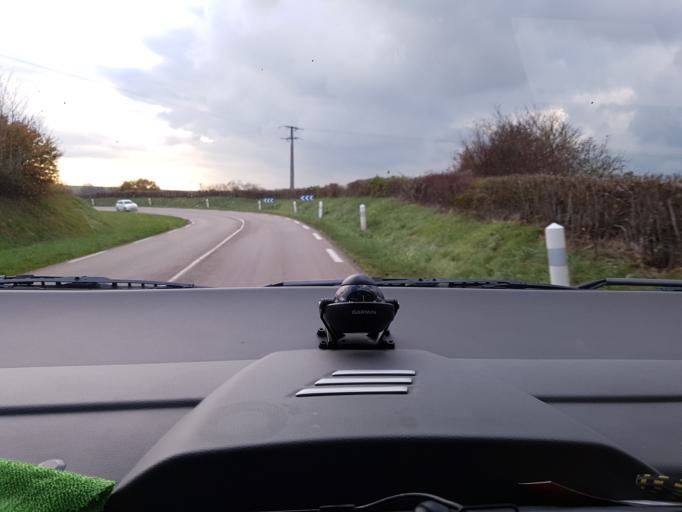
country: FR
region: Haute-Normandie
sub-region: Departement de la Seine-Maritime
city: Varengeville-sur-Mer
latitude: 49.8790
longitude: 0.9625
